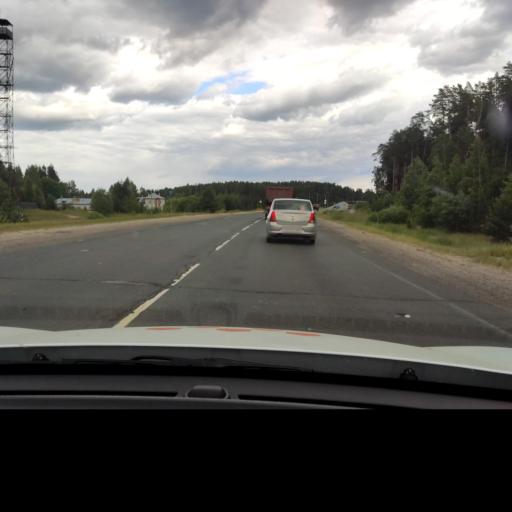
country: RU
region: Mariy-El
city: Yoshkar-Ola
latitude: 56.5422
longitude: 47.9747
